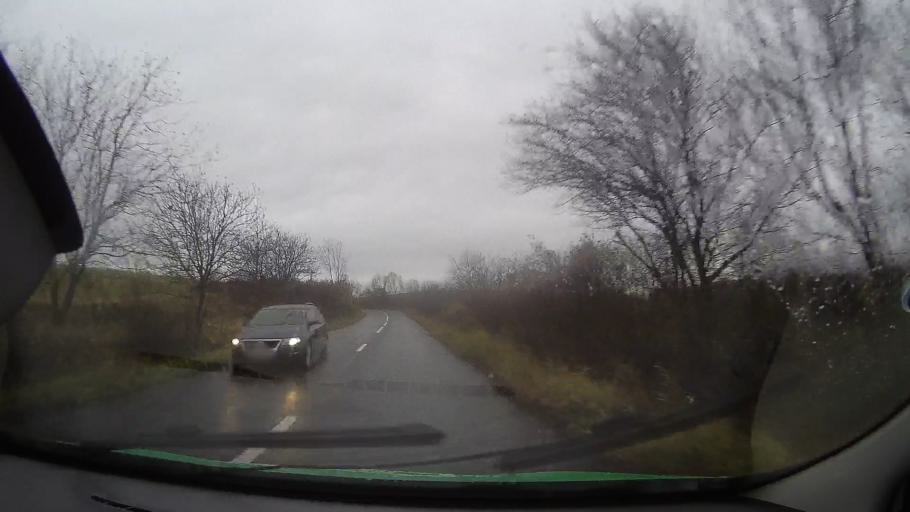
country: RO
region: Mures
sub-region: Comuna Brancovenesti
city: Valenii de Mures
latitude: 46.8997
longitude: 24.7921
